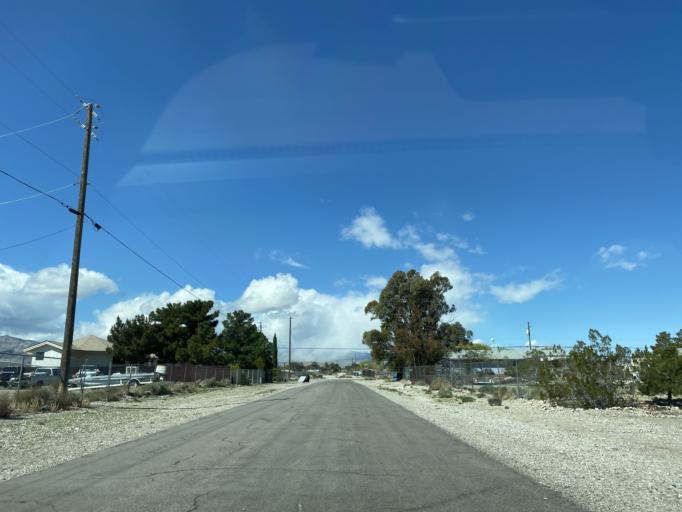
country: US
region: Nevada
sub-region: Clark County
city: North Las Vegas
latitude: 36.3249
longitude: -115.2816
